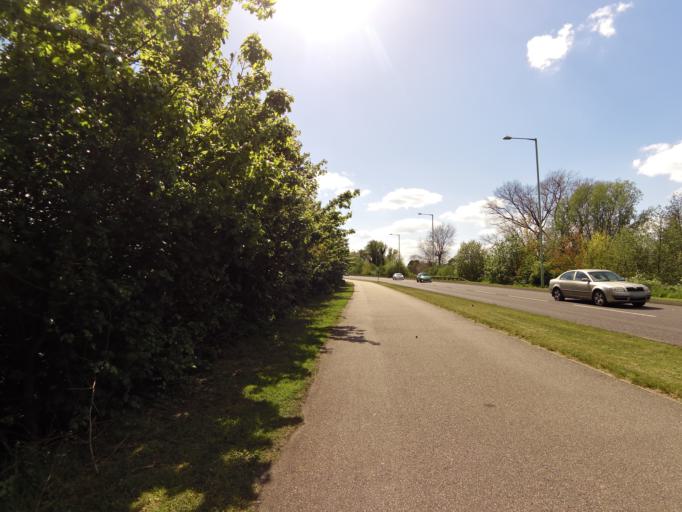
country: GB
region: England
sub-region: Suffolk
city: Lowestoft
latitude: 52.4618
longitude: 1.7270
